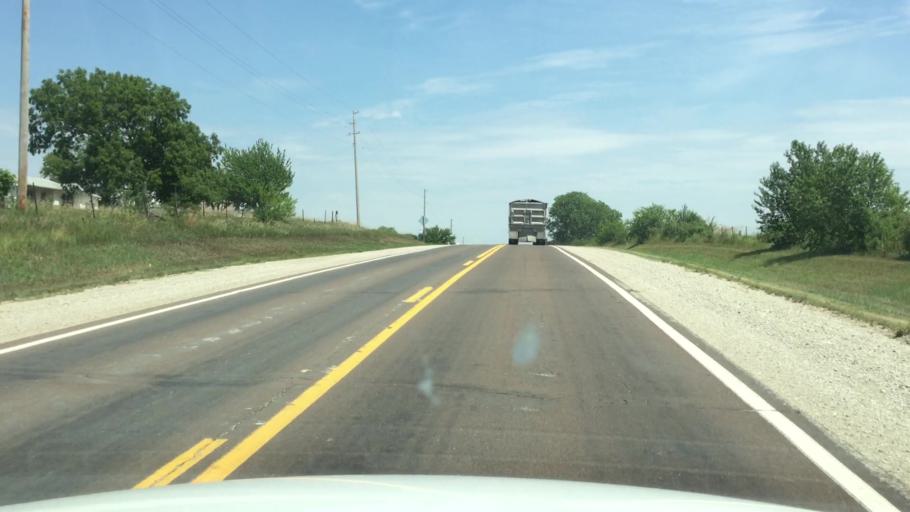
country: US
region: Kansas
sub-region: Shawnee County
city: Topeka
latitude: 38.9859
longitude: -95.5140
